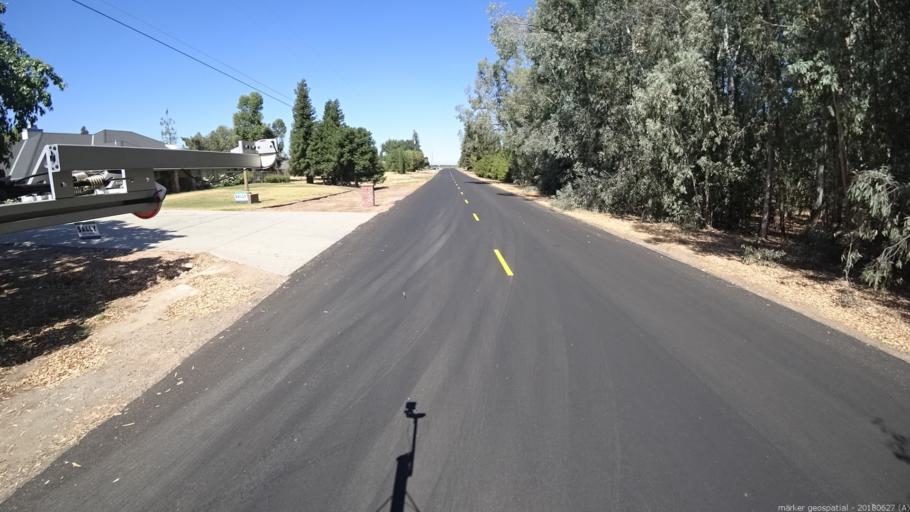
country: US
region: California
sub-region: Madera County
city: Bonadelle Ranchos-Madera Ranchos
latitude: 36.9179
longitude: -119.8907
